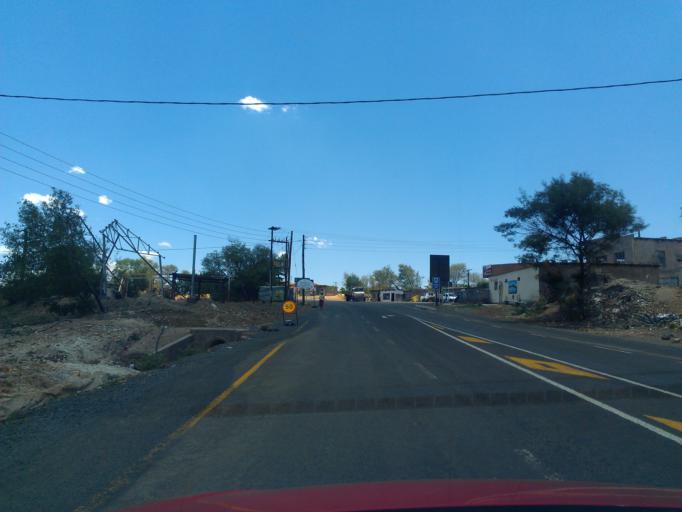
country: LS
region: Berea
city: Teyateyaneng
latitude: -29.1013
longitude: 27.9595
